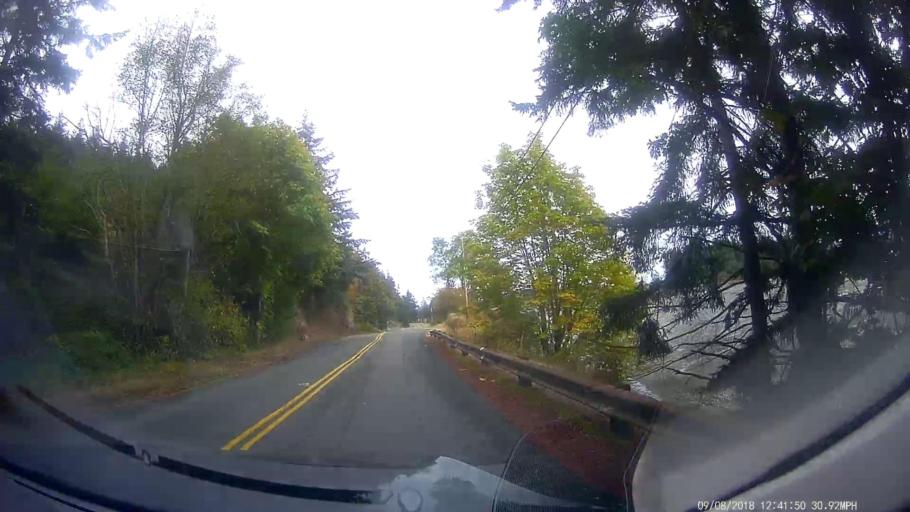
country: US
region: Washington
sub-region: Skagit County
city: Anacortes
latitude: 48.4785
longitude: -122.5922
